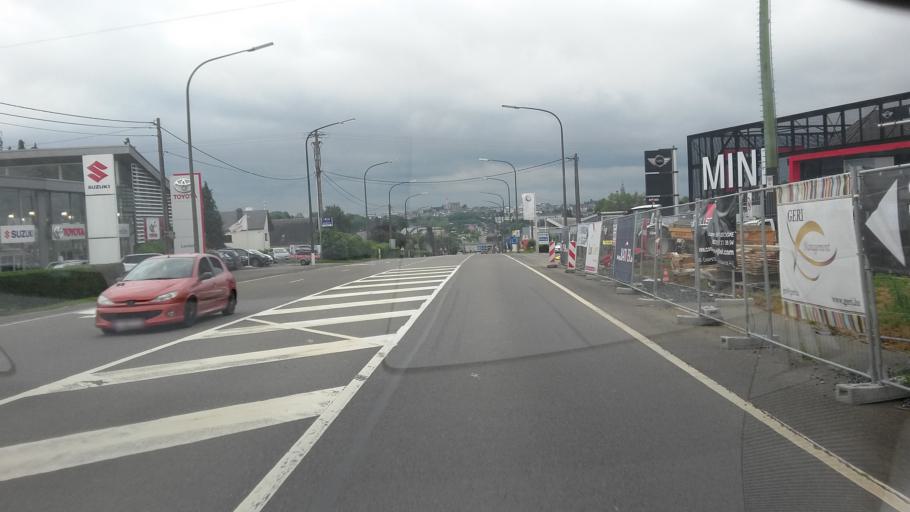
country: BE
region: Wallonia
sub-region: Province du Luxembourg
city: Arlon
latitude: 49.7050
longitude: 5.8052
